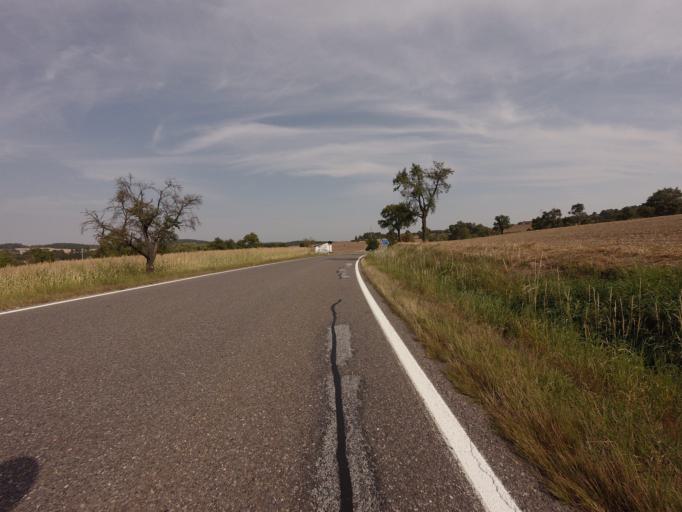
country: CZ
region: Central Bohemia
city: Petrovice
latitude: 49.5126
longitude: 14.3594
